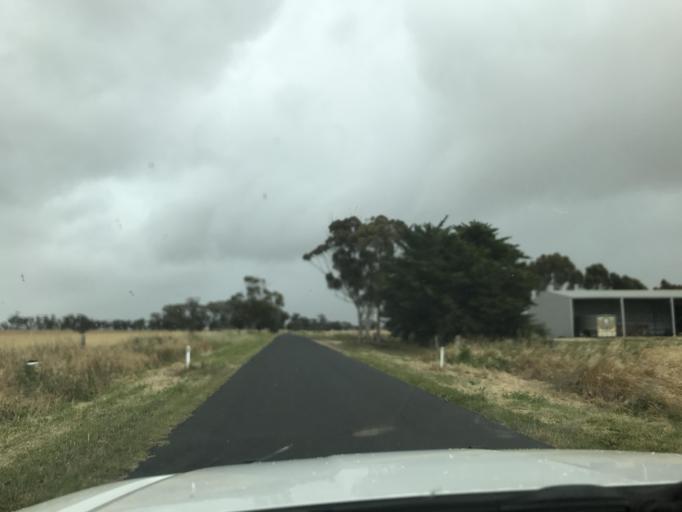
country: AU
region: South Australia
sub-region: Tatiara
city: Bordertown
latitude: -36.3435
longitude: 141.2232
